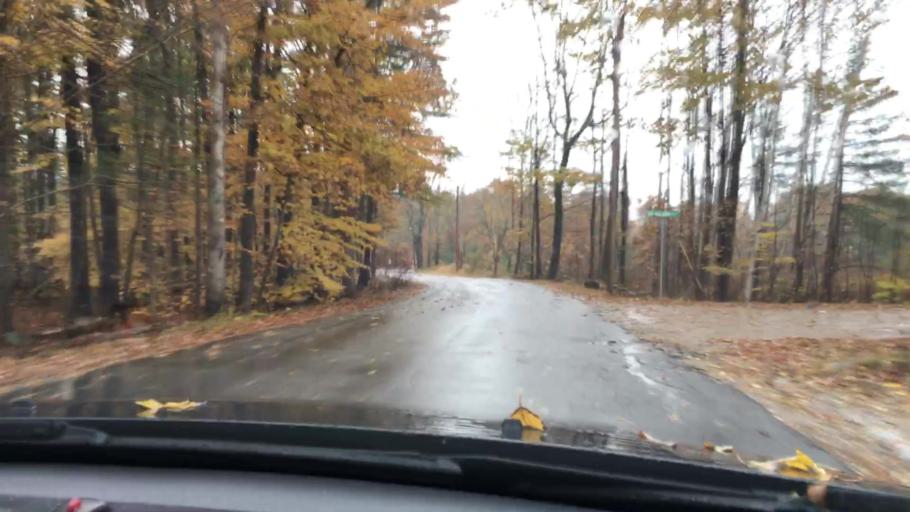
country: US
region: New Hampshire
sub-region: Belknap County
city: Meredith
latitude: 43.7016
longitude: -71.5111
